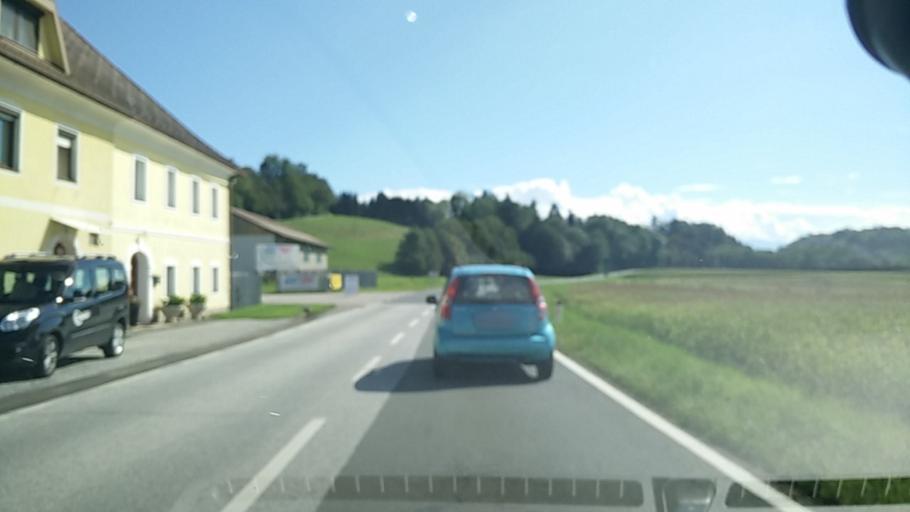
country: AT
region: Carinthia
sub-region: Politischer Bezirk Sankt Veit an der Glan
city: Sankt Veit an der Glan
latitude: 46.7351
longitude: 14.3927
